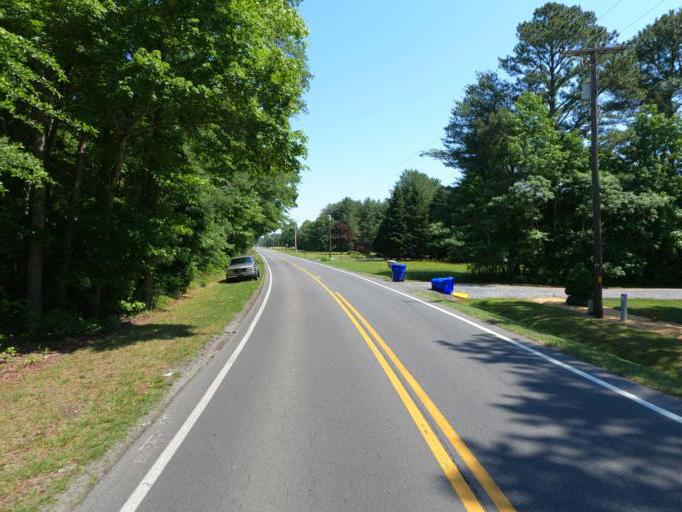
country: US
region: Delaware
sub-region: Sussex County
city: Georgetown
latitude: 38.6892
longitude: -75.3456
